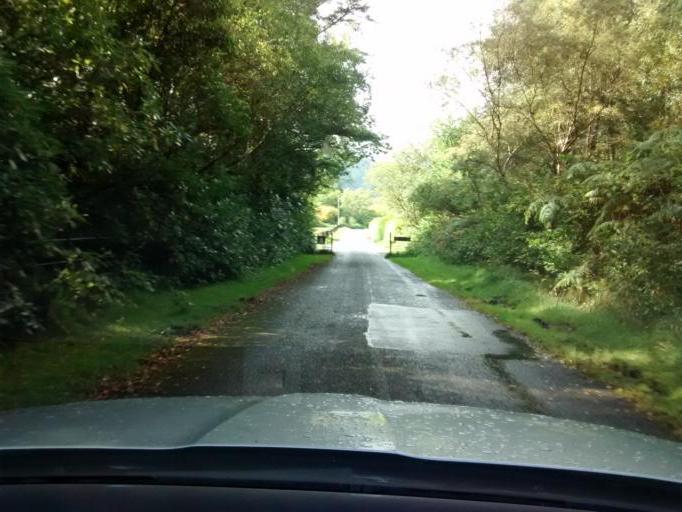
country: GB
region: Scotland
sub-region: North Ayrshire
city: Isle of Arran
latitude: 55.5936
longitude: -5.1609
